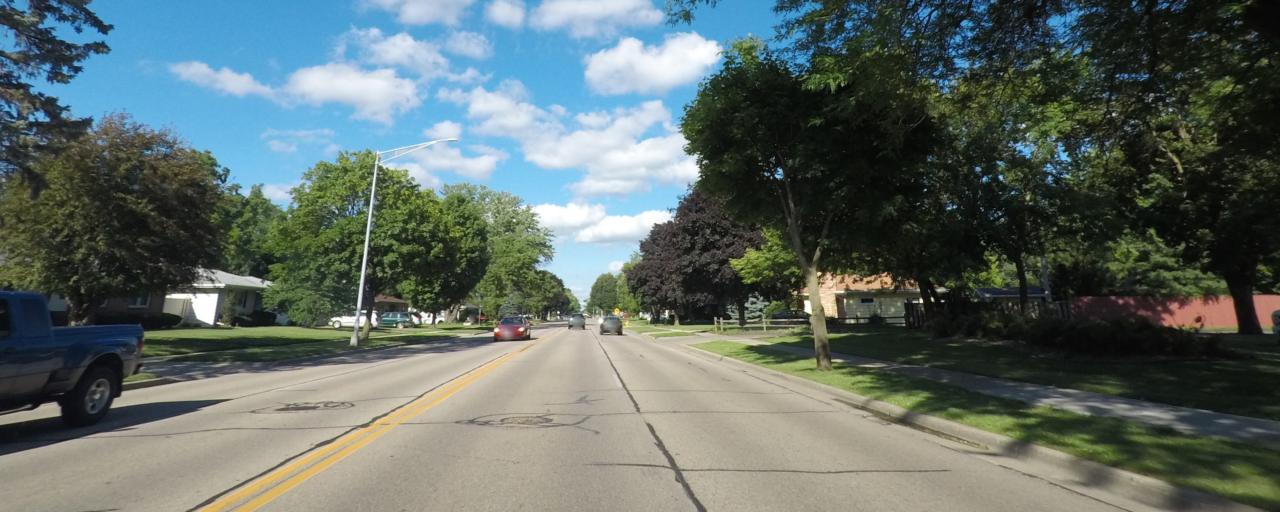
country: US
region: Wisconsin
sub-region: Rock County
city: Janesville
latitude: 42.6931
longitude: -88.9961
